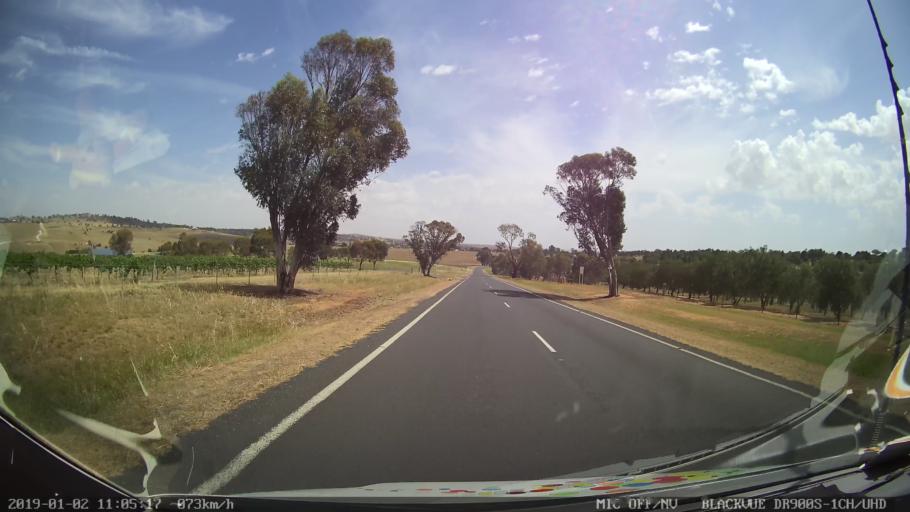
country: AU
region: New South Wales
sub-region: Young
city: Young
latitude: -34.5666
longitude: 148.3541
